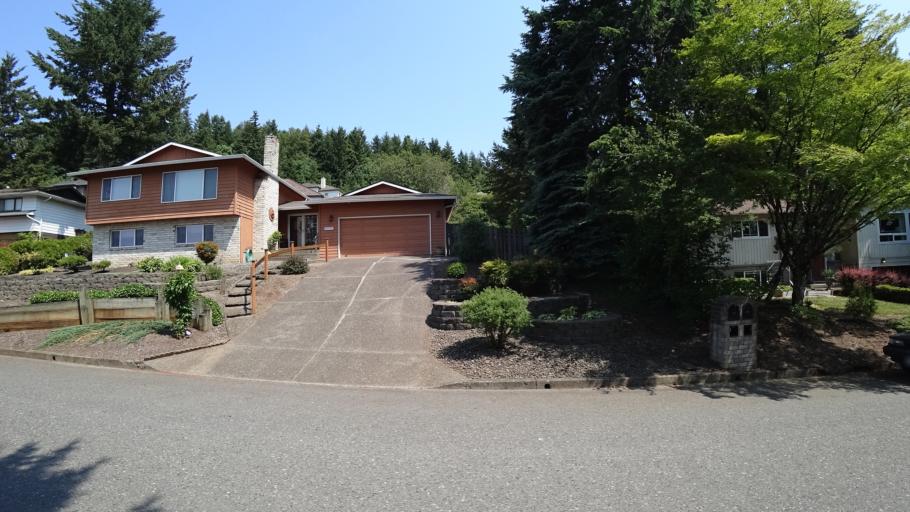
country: US
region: Oregon
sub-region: Multnomah County
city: Lents
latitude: 45.4523
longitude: -122.5588
